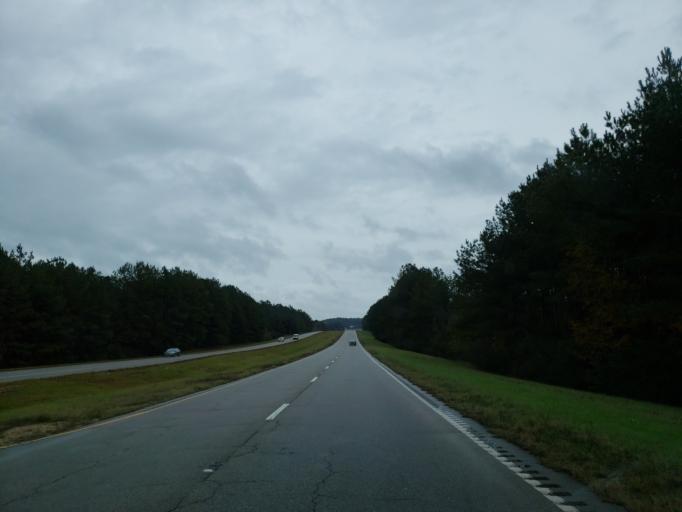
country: US
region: Mississippi
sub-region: Jones County
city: Laurel
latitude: 31.7029
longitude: -89.0842
